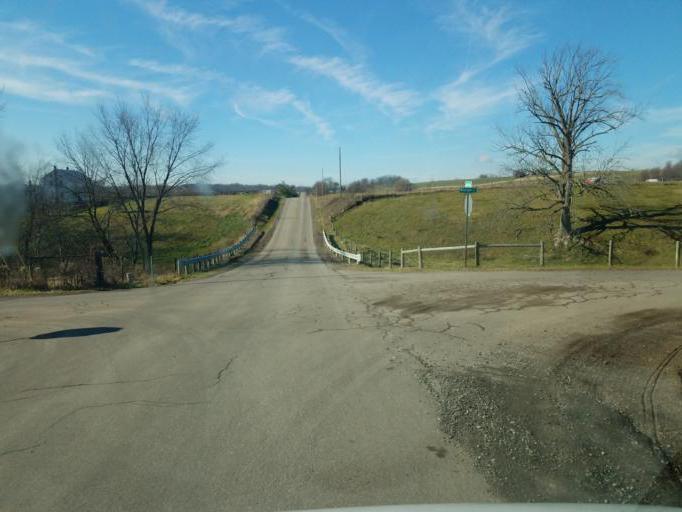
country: US
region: Ohio
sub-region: Wayne County
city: Dalton
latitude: 40.7338
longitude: -81.7065
